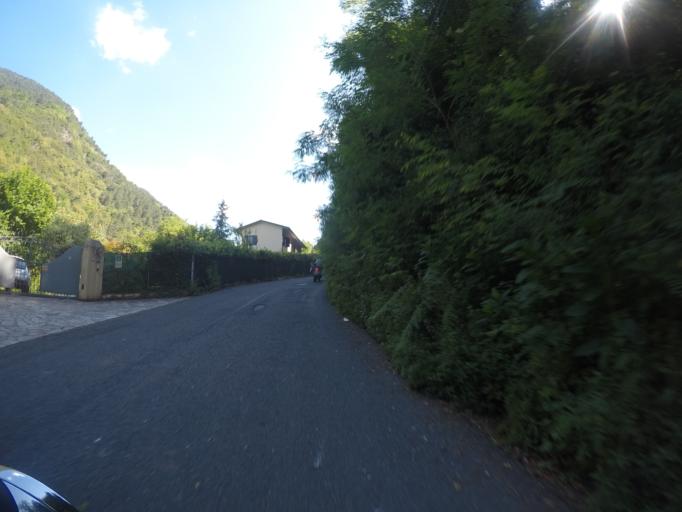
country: IT
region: Tuscany
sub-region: Provincia di Massa-Carrara
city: Montignoso
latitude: 44.0489
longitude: 10.1596
